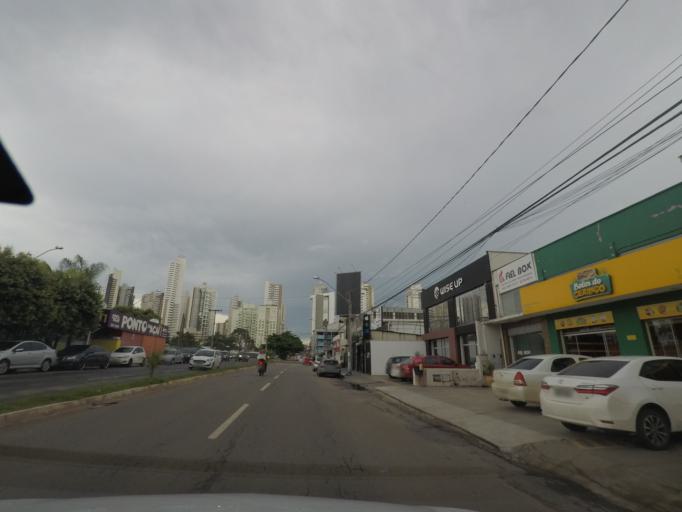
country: BR
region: Goias
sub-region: Goiania
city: Goiania
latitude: -16.7076
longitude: -49.2404
